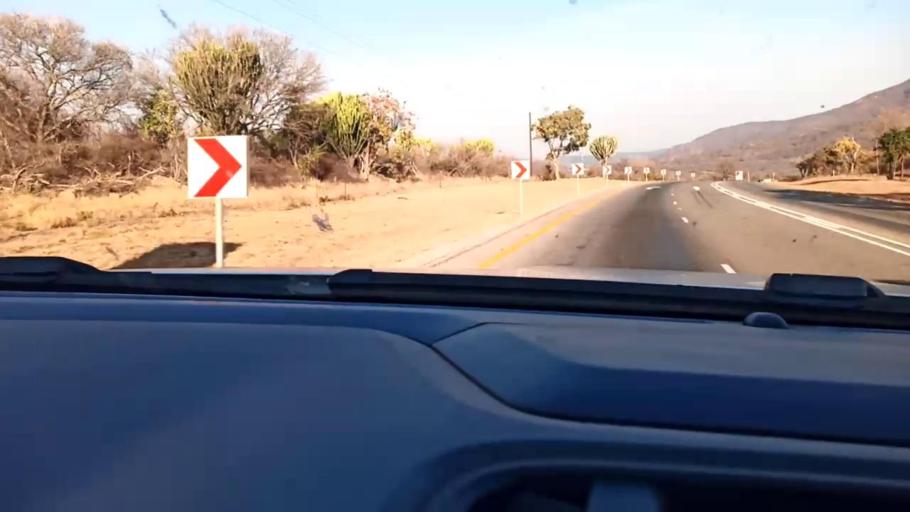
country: ZA
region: Limpopo
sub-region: Mopani District Municipality
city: Duiwelskloof
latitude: -23.6211
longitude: 30.1264
